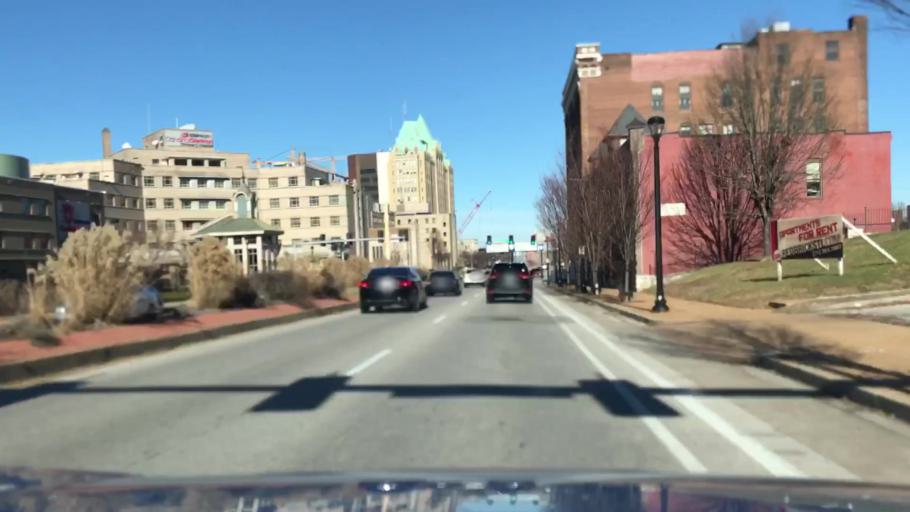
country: US
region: Missouri
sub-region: City of Saint Louis
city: St. Louis
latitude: 38.6198
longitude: -90.2387
